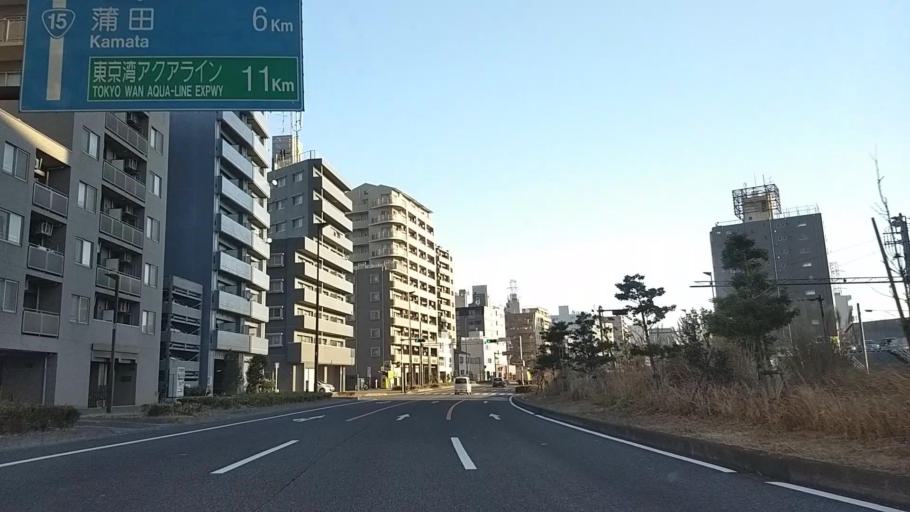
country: JP
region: Kanagawa
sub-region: Kawasaki-shi
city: Kawasaki
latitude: 35.5196
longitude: 139.6897
